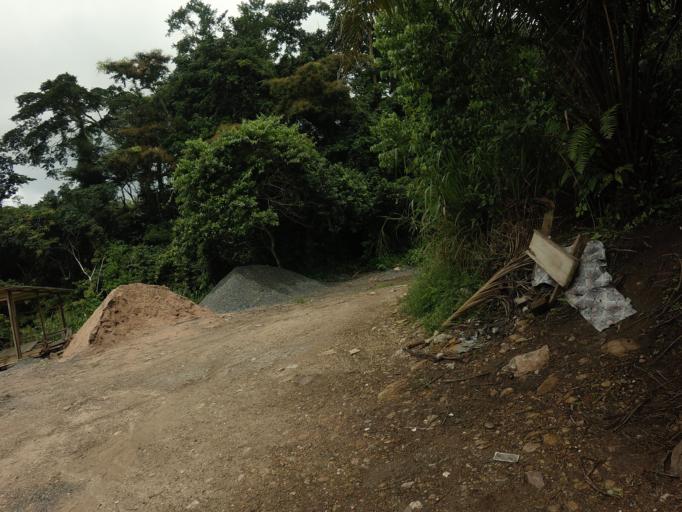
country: TG
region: Plateaux
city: Kpalime
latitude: 6.8427
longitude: 0.4463
